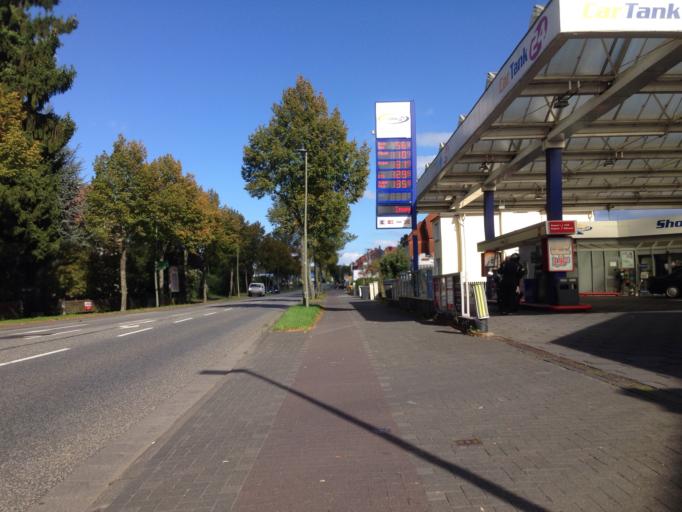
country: DE
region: Hesse
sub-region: Regierungsbezirk Giessen
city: Giessen
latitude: 50.6043
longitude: 8.6932
